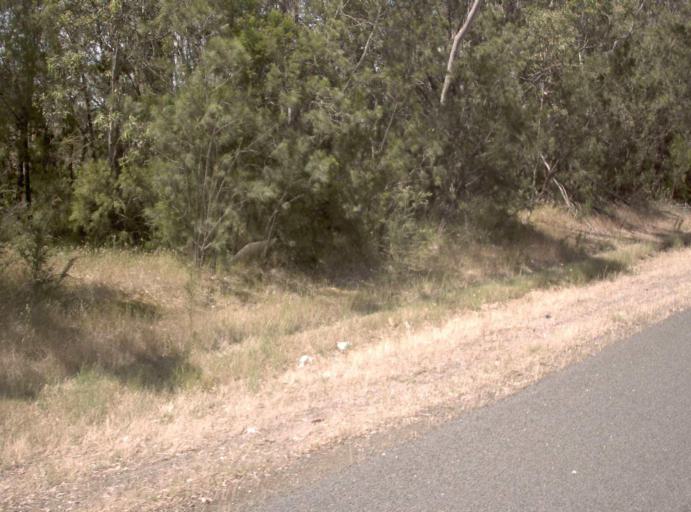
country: AU
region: Victoria
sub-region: Wellington
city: Sale
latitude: -37.9431
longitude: 147.1337
